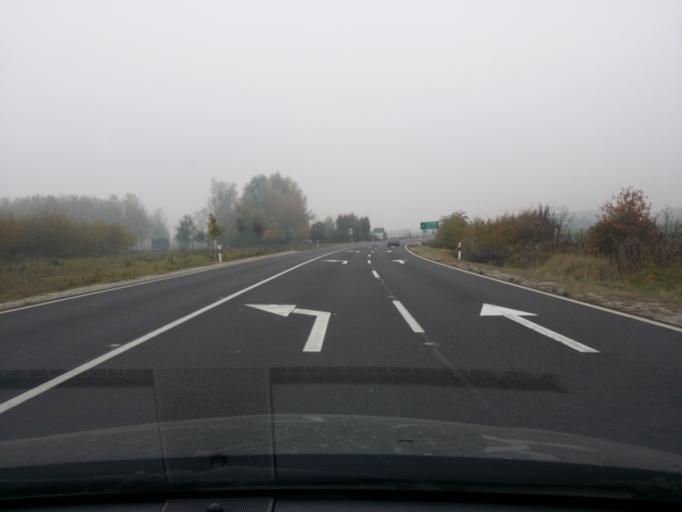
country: HU
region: Szabolcs-Szatmar-Bereg
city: Nyirbogdany
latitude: 48.0413
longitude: 21.8635
